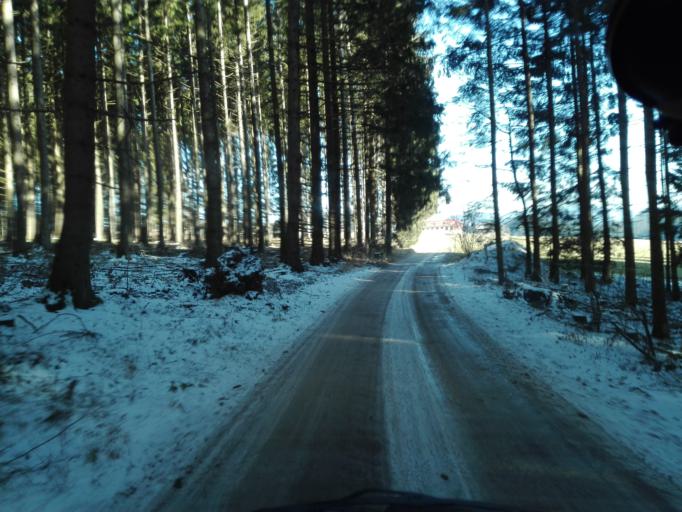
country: AT
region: Upper Austria
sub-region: Politischer Bezirk Urfahr-Umgebung
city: Sonnberg im Muehlkreis
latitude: 48.4614
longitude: 14.3195
